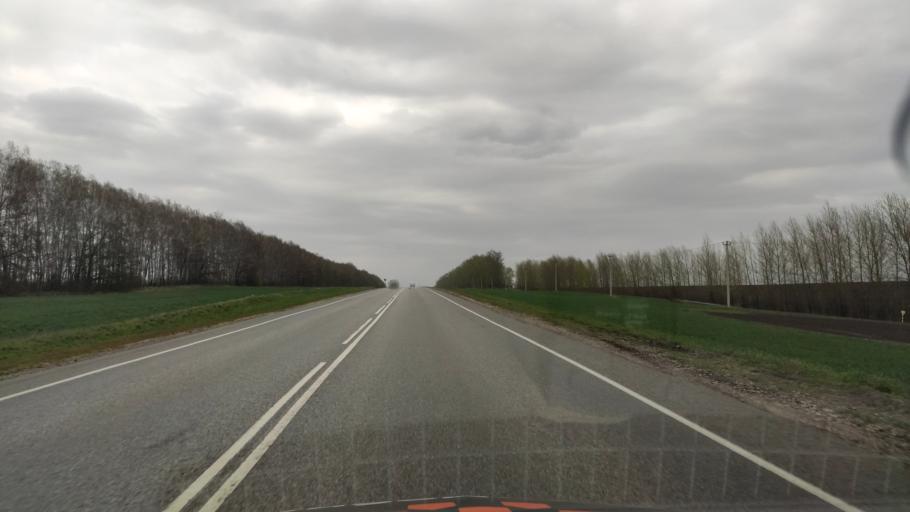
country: RU
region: Kursk
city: Gorshechnoye
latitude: 51.5488
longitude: 38.1277
